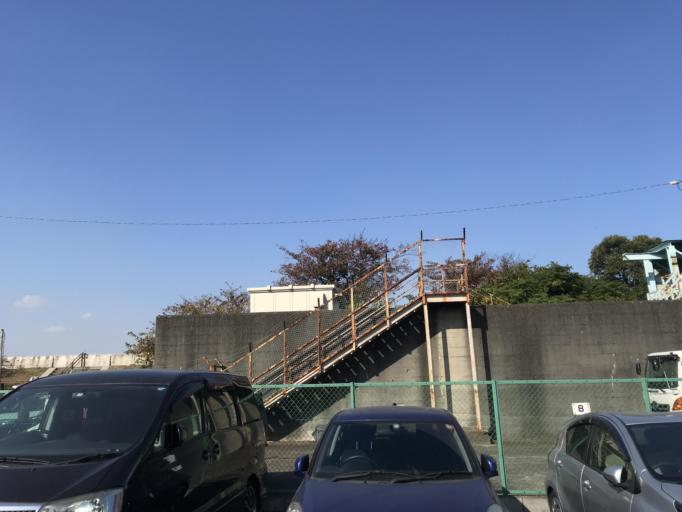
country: JP
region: Kanagawa
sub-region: Kawasaki-shi
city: Kawasaki
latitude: 35.5404
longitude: 139.7494
